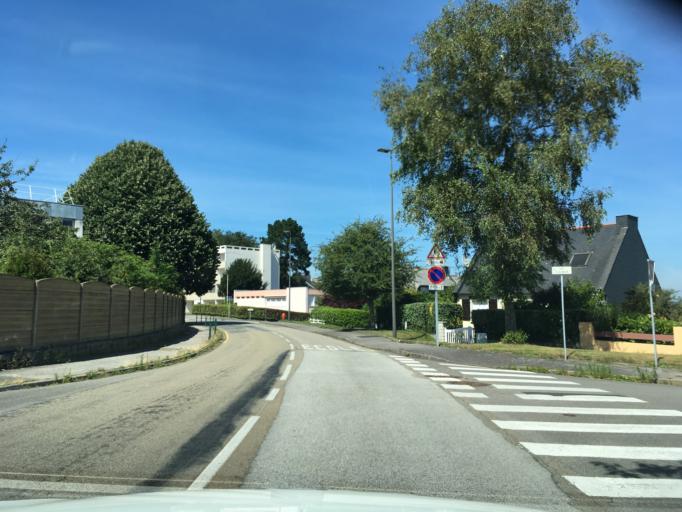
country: FR
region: Brittany
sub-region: Departement du Finistere
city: Quimper
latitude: 47.9841
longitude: -4.1236
